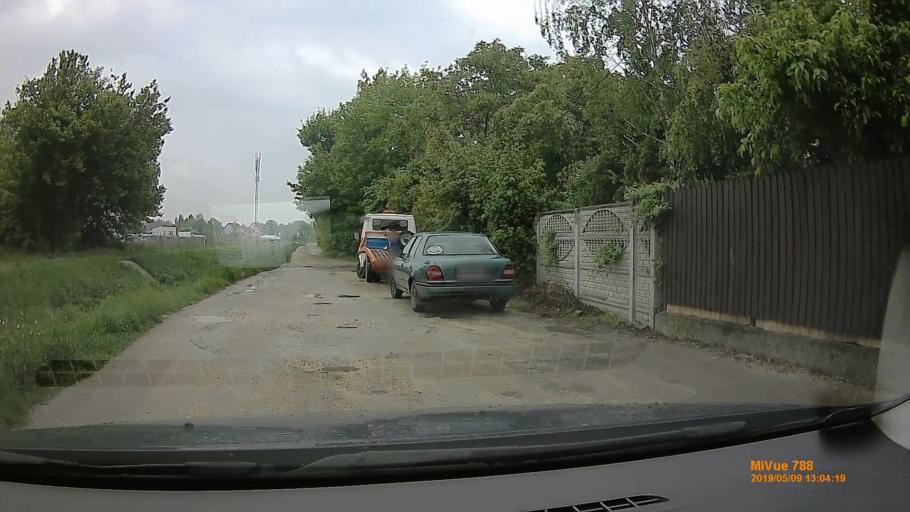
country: HU
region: Budapest
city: Budapest XVI. keruelet
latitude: 47.5357
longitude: 19.1769
